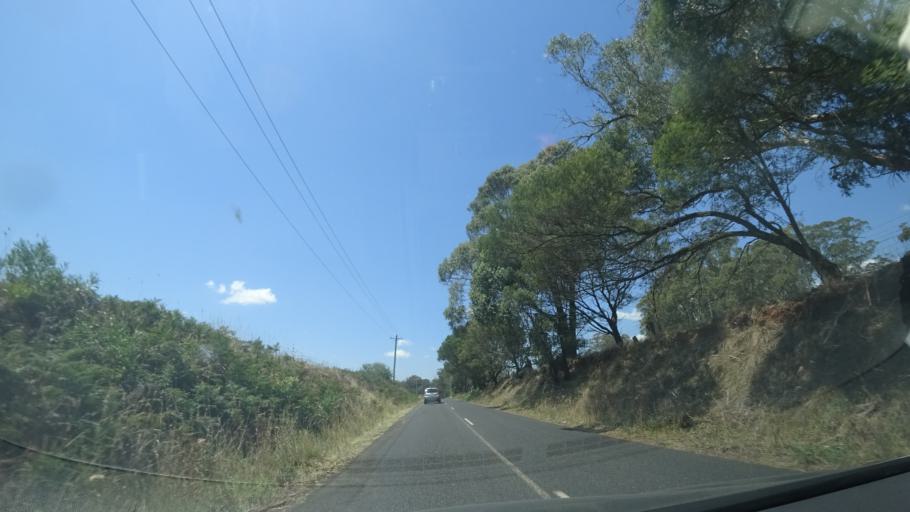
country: AU
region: New South Wales
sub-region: Wingecarribee
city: Bundanoon
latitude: -34.6103
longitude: 150.2669
